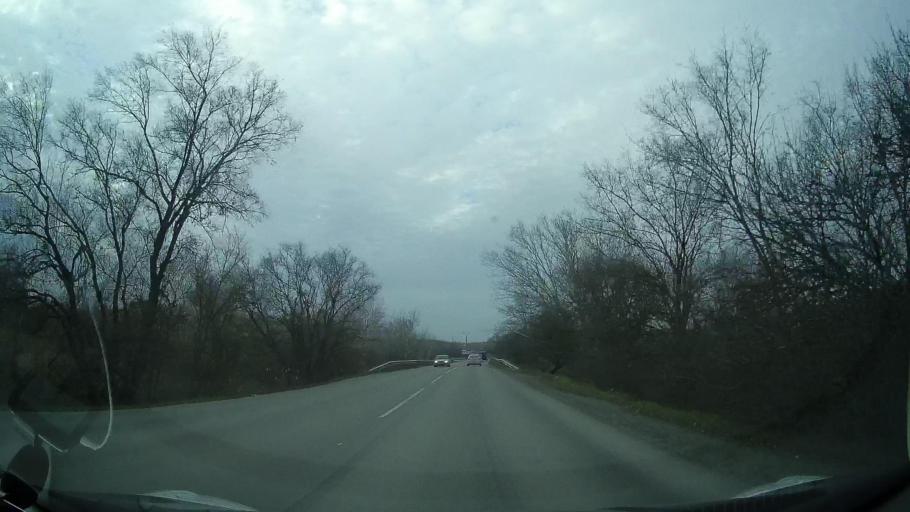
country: RU
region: Rostov
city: Aksay
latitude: 47.2371
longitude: 39.8606
